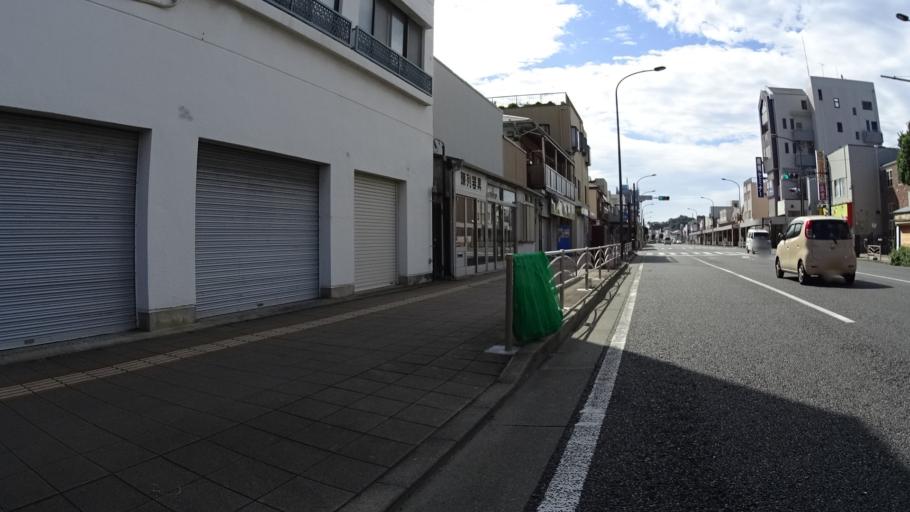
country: JP
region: Kanagawa
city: Yokosuka
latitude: 35.2716
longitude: 139.6780
